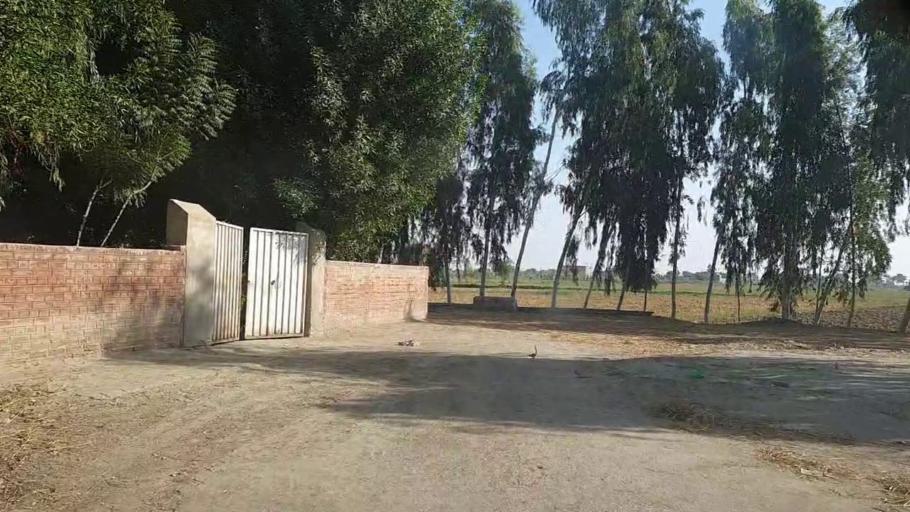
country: PK
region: Sindh
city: Tangwani
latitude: 28.2843
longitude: 69.0018
